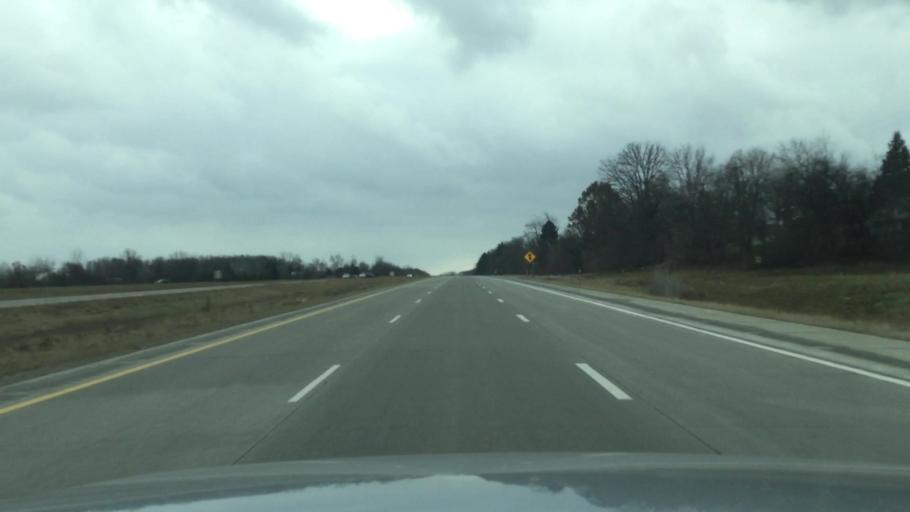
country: US
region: Michigan
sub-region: Genesee County
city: Grand Blanc
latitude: 42.9432
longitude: -83.6818
